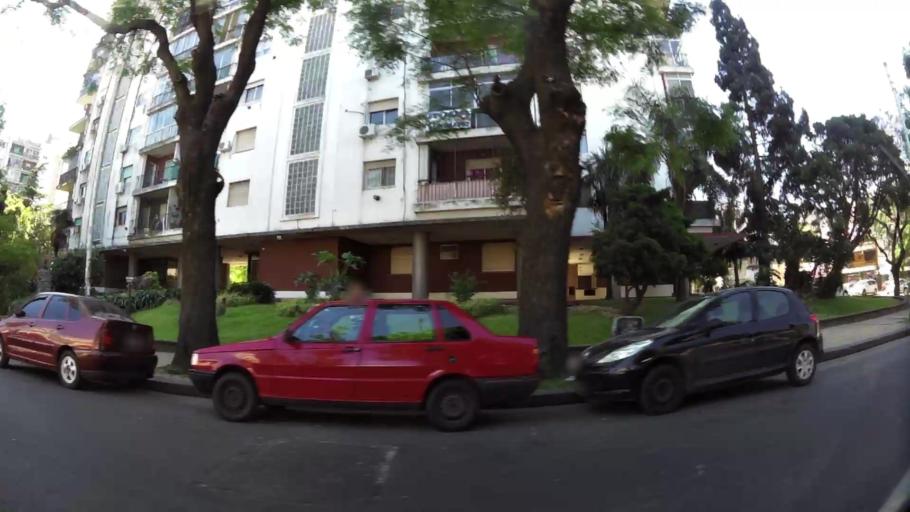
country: AR
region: Buenos Aires F.D.
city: Villa Santa Rita
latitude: -34.6352
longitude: -58.4480
